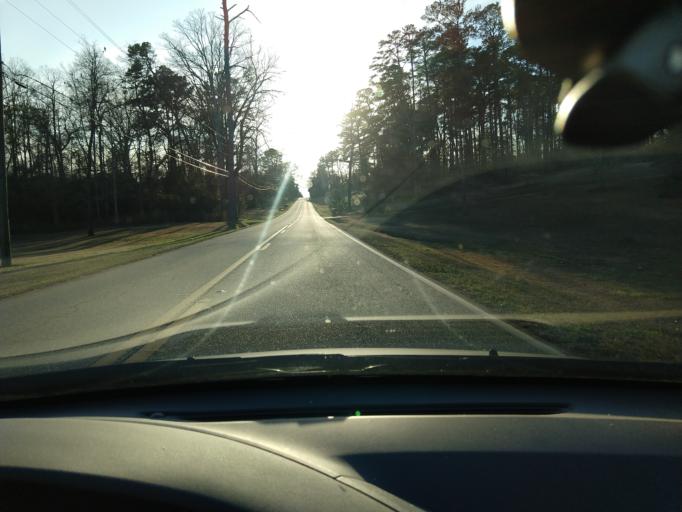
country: US
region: Georgia
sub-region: Sumter County
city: Americus
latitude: 32.0864
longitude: -84.1993
